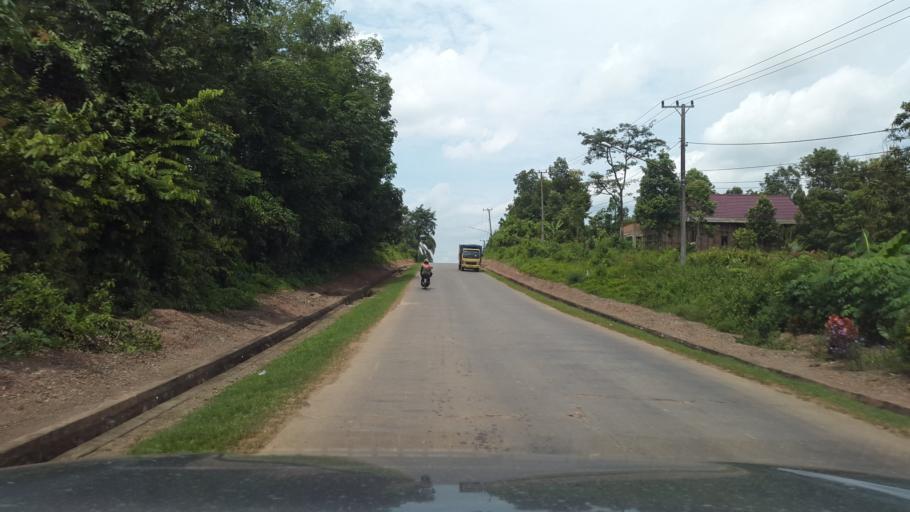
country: ID
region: South Sumatra
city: Gunungmegang Dalam
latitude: -3.3054
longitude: 103.8653
